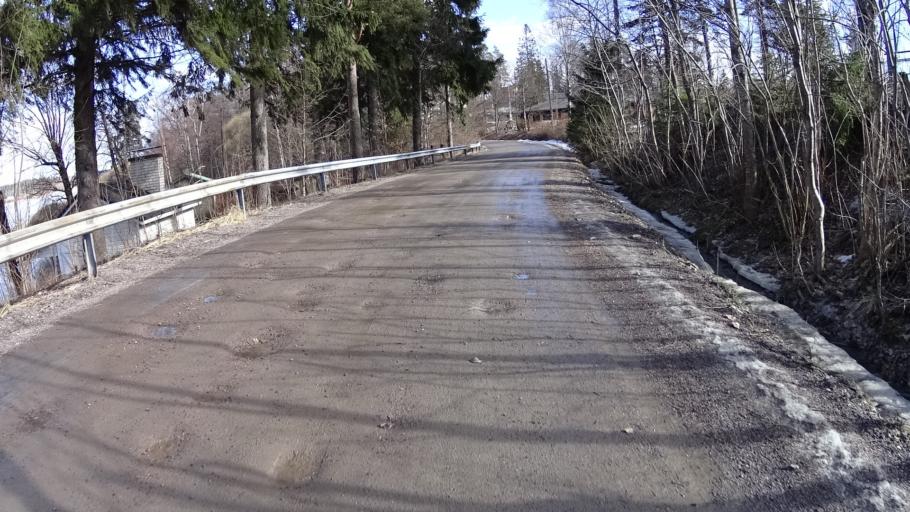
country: FI
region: Uusimaa
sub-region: Helsinki
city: Kilo
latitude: 60.2594
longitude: 24.7617
